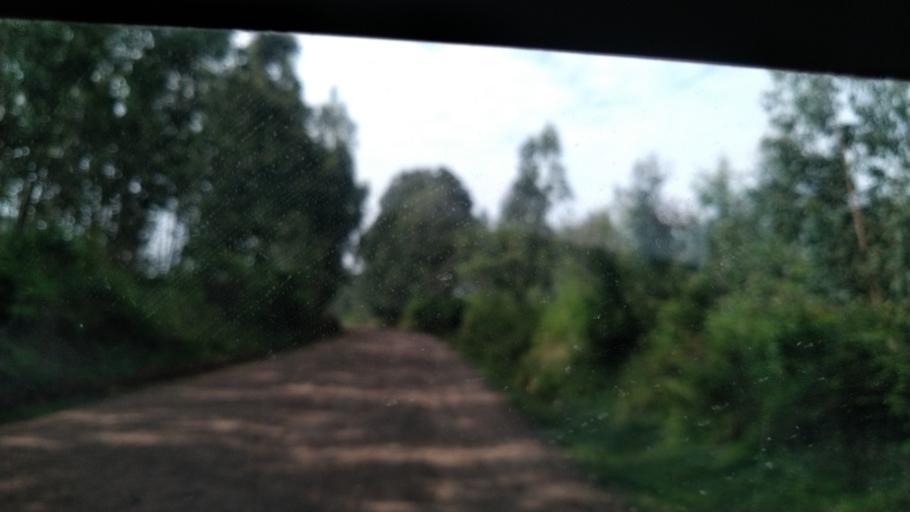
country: ET
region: Oromiya
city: Jima
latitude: 7.6662
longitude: 37.2450
